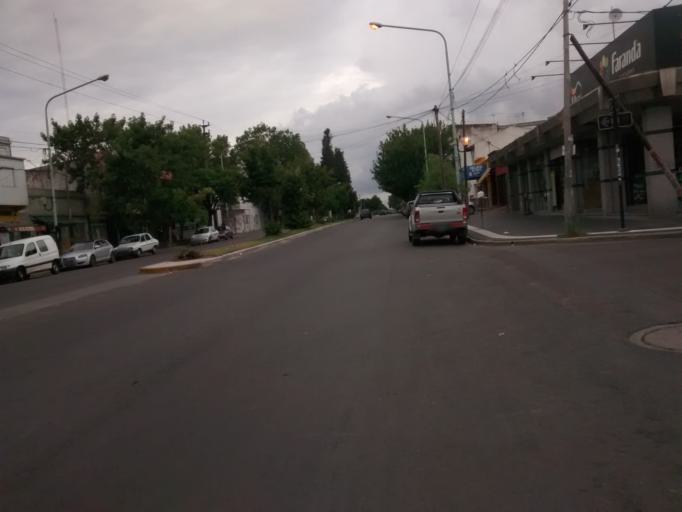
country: AR
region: Buenos Aires
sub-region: Partido de La Plata
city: La Plata
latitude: -34.9345
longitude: -57.9233
